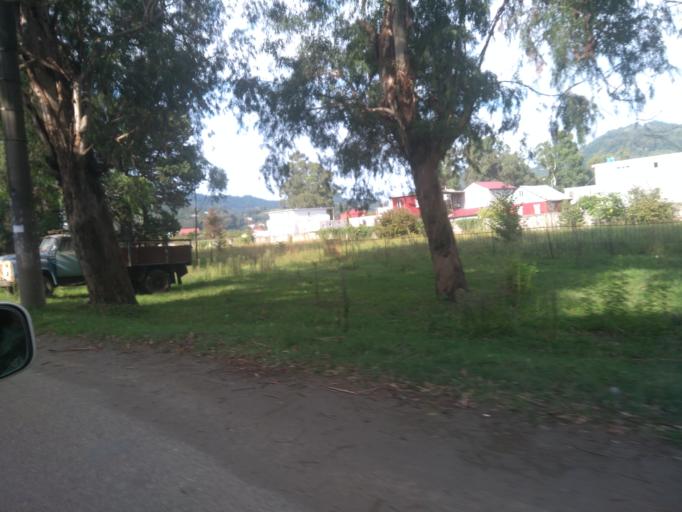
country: GE
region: Ajaria
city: Khelvachauri
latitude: 41.5846
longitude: 41.6526
